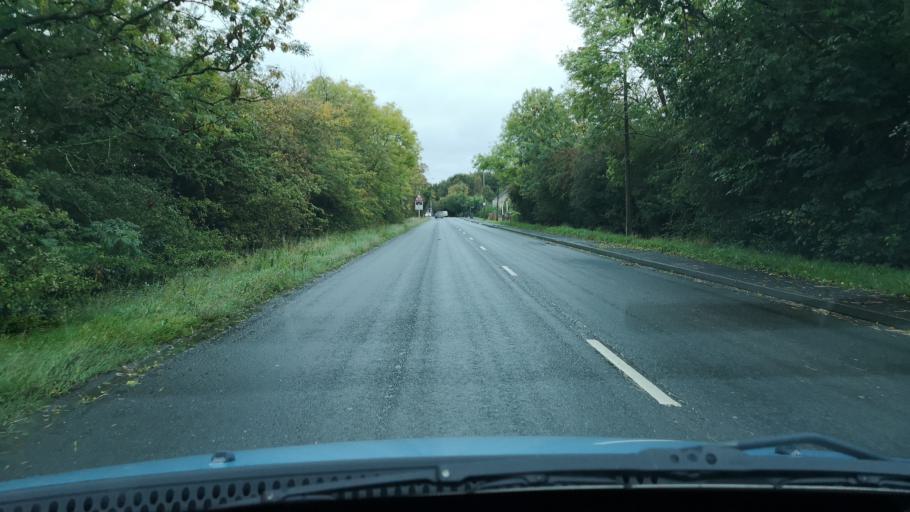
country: GB
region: England
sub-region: Doncaster
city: Askern
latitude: 53.6244
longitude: -1.1515
